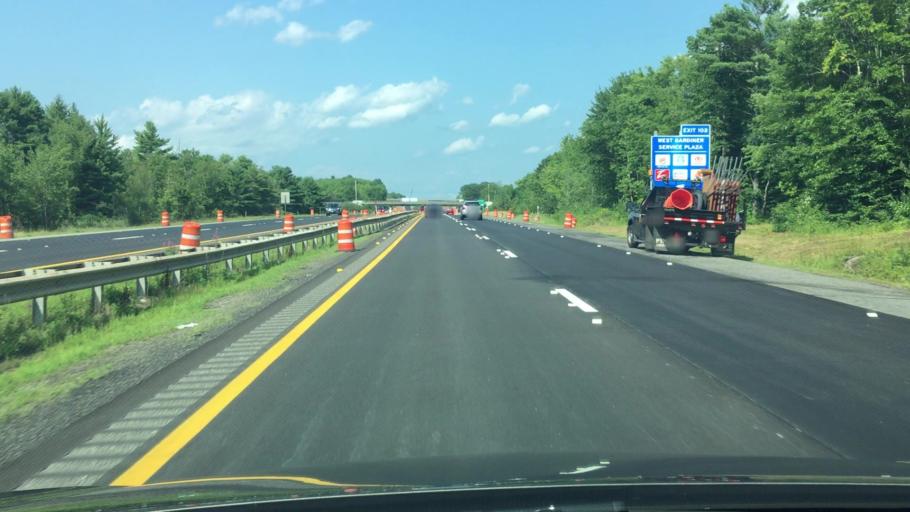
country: US
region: Maine
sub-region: Kennebec County
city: Gardiner
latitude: 44.2050
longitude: -69.8358
